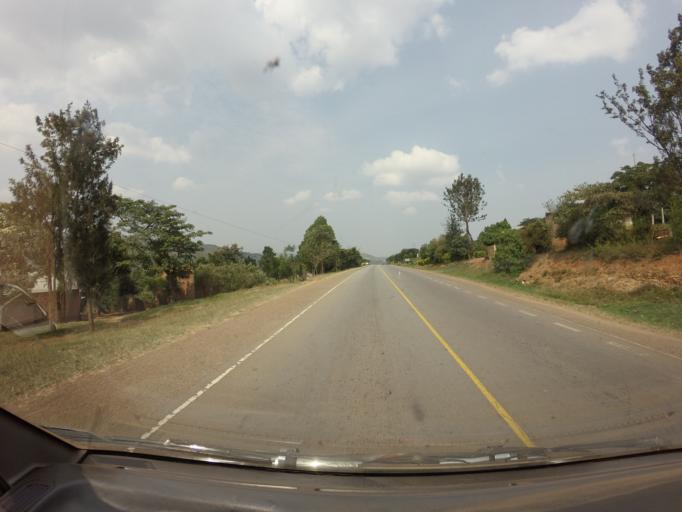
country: UG
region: Central Region
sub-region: Lwengo District
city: Lwengo
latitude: -0.3808
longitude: 31.3029
